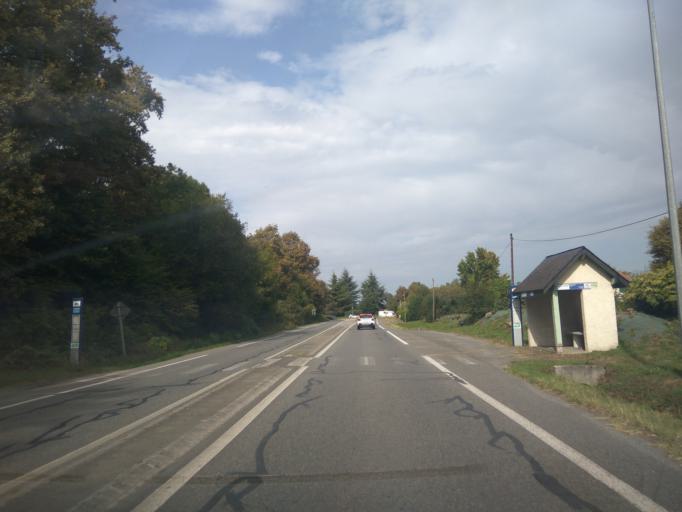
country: FR
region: Aquitaine
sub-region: Departement des Pyrenees-Atlantiques
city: Artiguelouve
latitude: 43.3145
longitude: -0.4549
